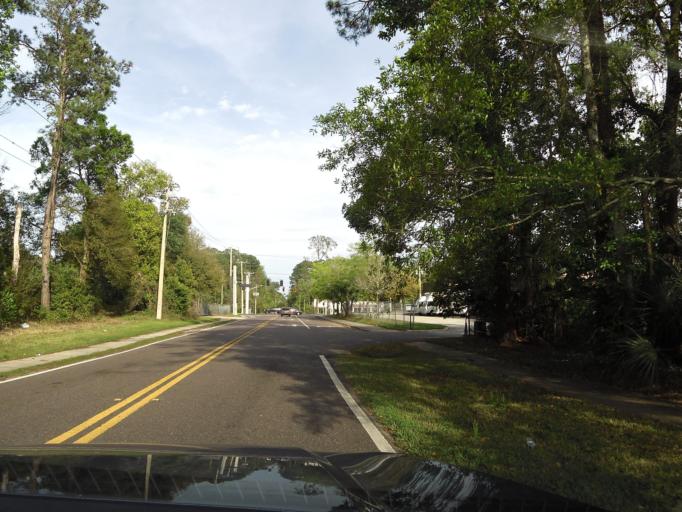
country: US
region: Florida
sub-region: Clay County
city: Bellair-Meadowbrook Terrace
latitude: 30.2262
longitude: -81.7392
